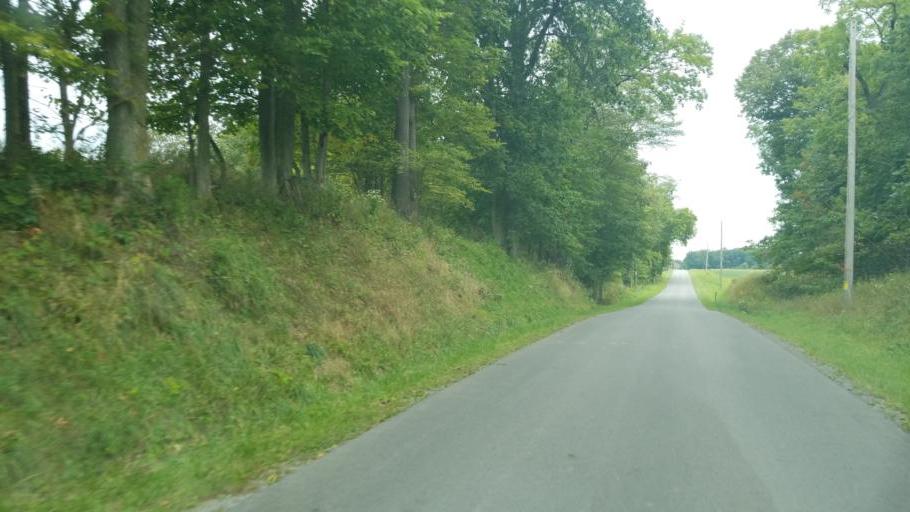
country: US
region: Ohio
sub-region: Wyandot County
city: Upper Sandusky
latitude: 40.7639
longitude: -83.1883
